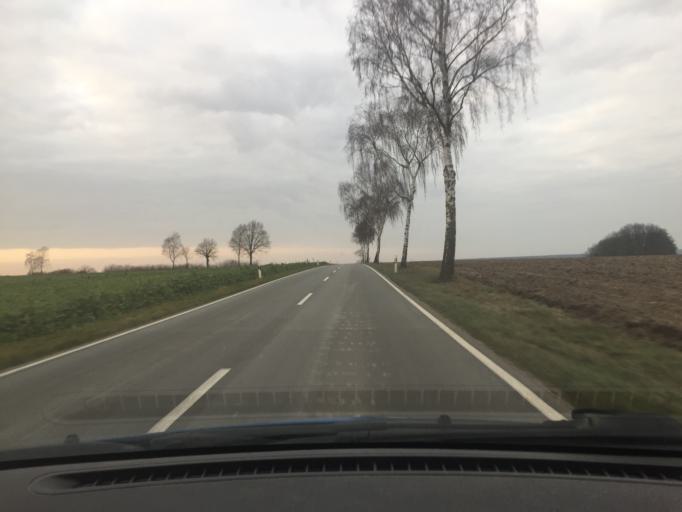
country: DE
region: Lower Saxony
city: Oetzen
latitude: 53.0440
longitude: 10.6462
